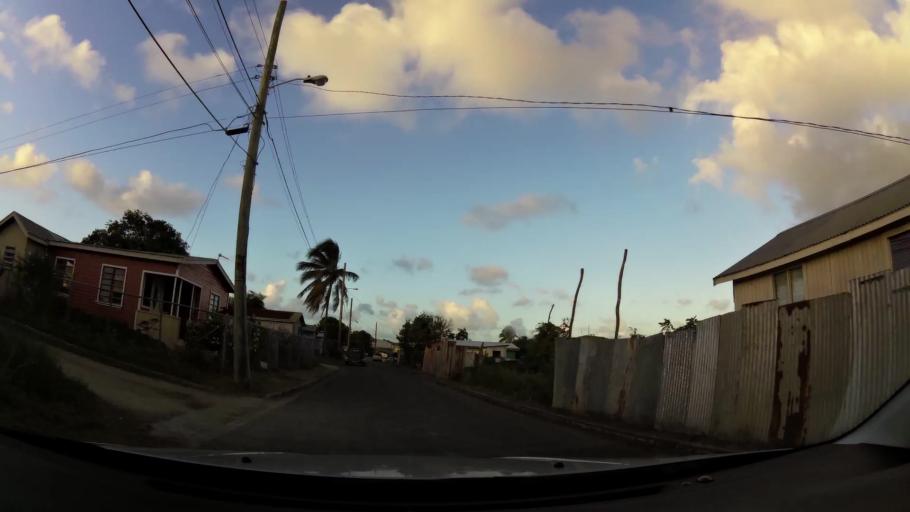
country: AG
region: Saint John
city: Saint John's
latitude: 17.1333
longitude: -61.8421
